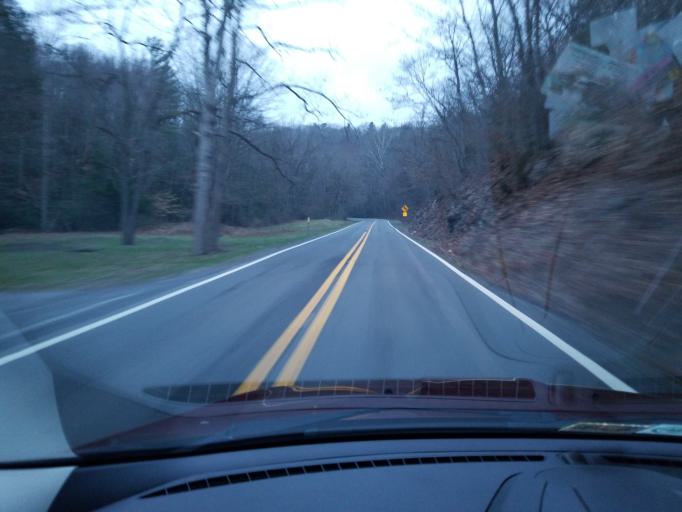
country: US
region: West Virginia
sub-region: Greenbrier County
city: Ronceverte
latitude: 37.7484
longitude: -80.4080
